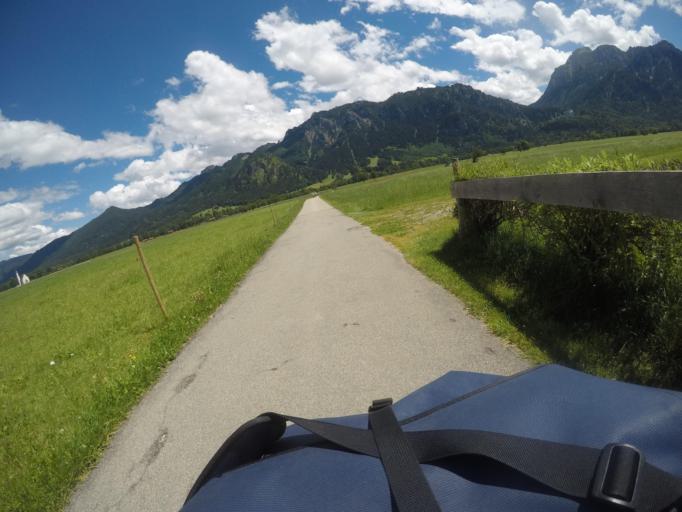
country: DE
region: Bavaria
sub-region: Swabia
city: Schwangau
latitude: 47.5754
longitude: 10.7402
